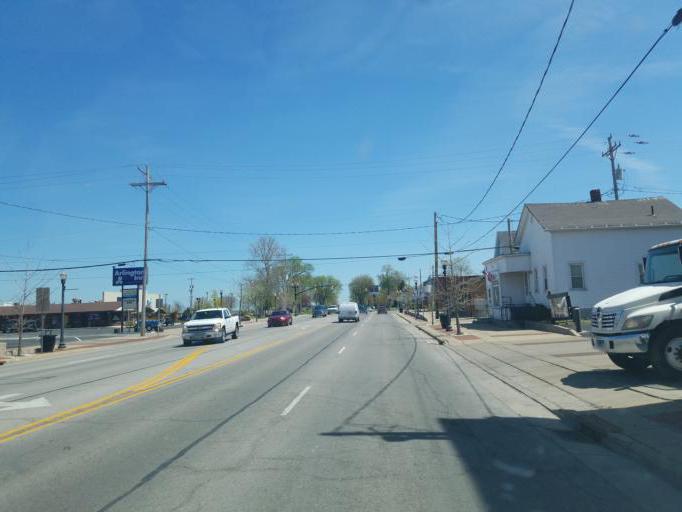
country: US
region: Ohio
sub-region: Ottawa County
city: Port Clinton
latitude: 41.5133
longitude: -82.9408
